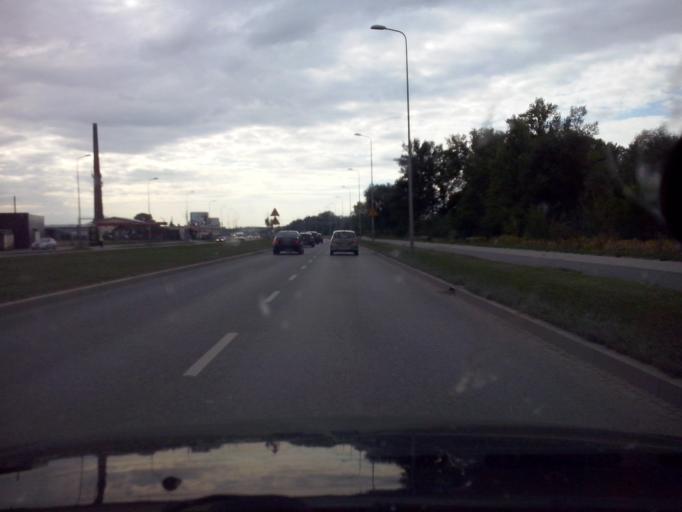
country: PL
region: Lesser Poland Voivodeship
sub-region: Powiat wielicki
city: Czarnochowice
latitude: 50.0388
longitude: 20.0368
